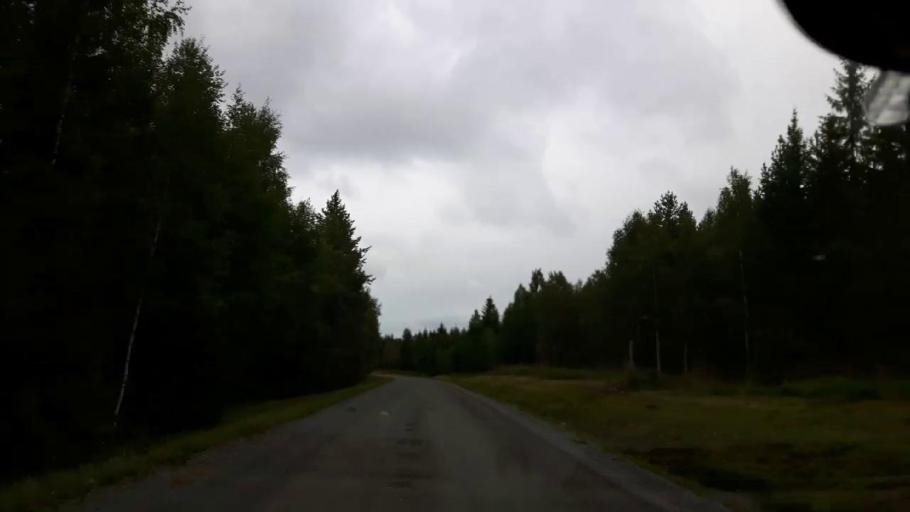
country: SE
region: Jaemtland
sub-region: OEstersunds Kommun
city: Ostersund
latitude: 63.0667
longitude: 14.5524
